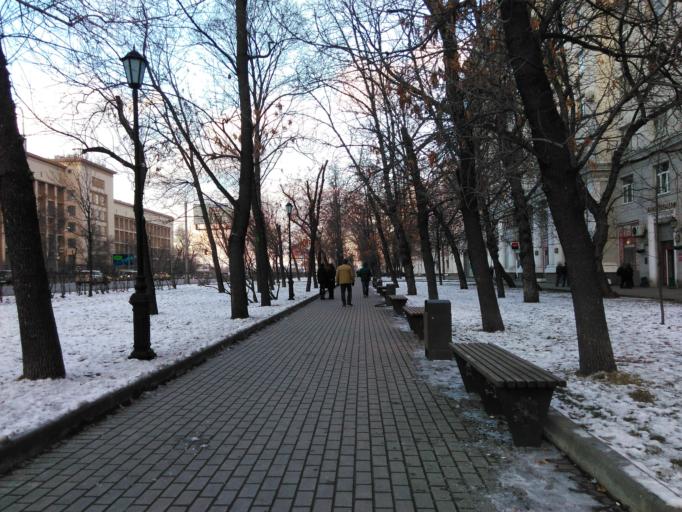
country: RU
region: Moscow
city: Mar'ina Roshcha
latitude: 55.8138
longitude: 37.6388
